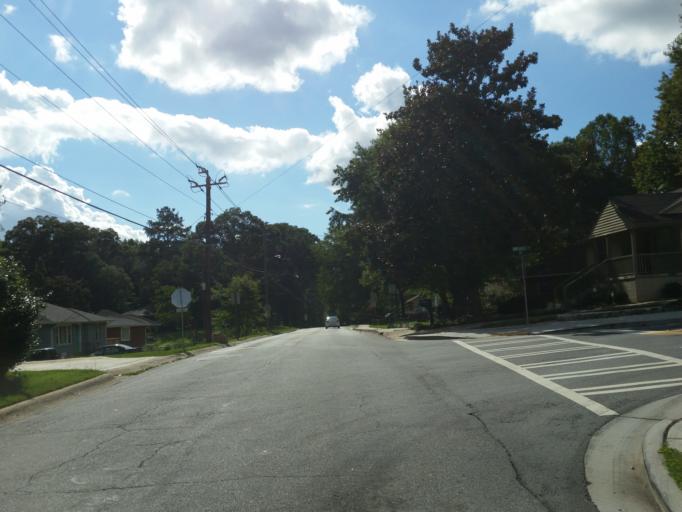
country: US
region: Georgia
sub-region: Cobb County
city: Smyrna
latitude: 33.8872
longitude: -84.5269
